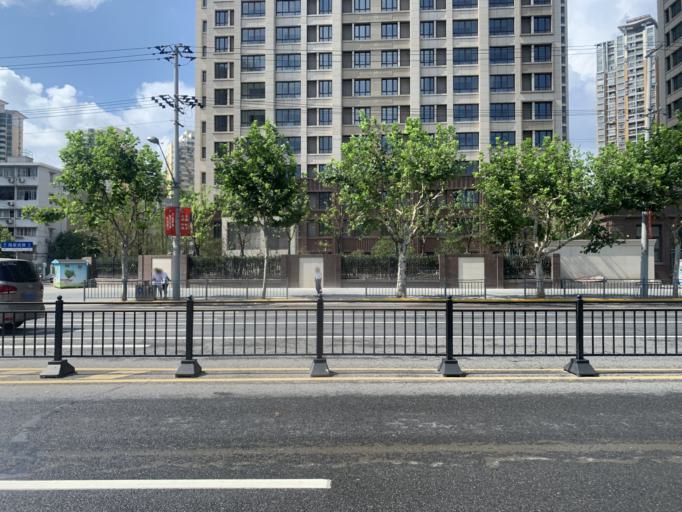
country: CN
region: Shanghai Shi
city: Luwan
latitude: 31.2145
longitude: 121.4876
